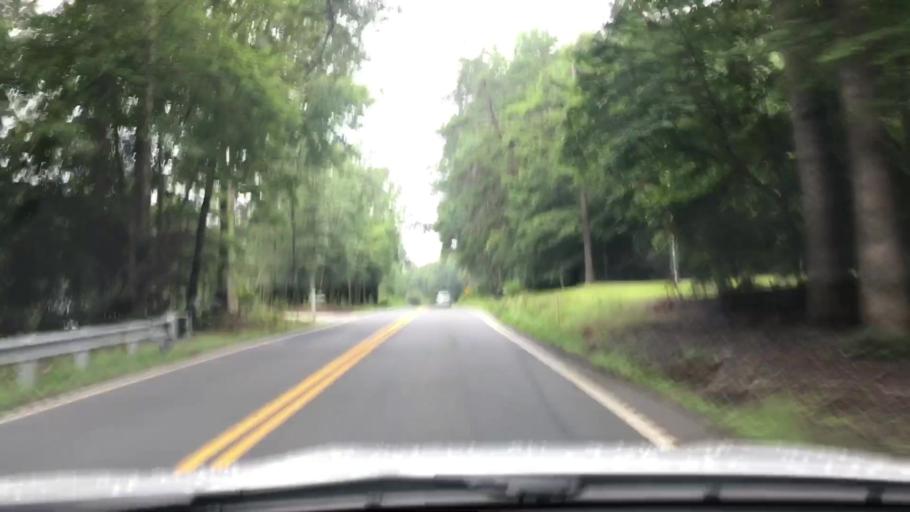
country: US
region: South Carolina
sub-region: Spartanburg County
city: Roebuck
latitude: 34.8255
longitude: -81.9453
